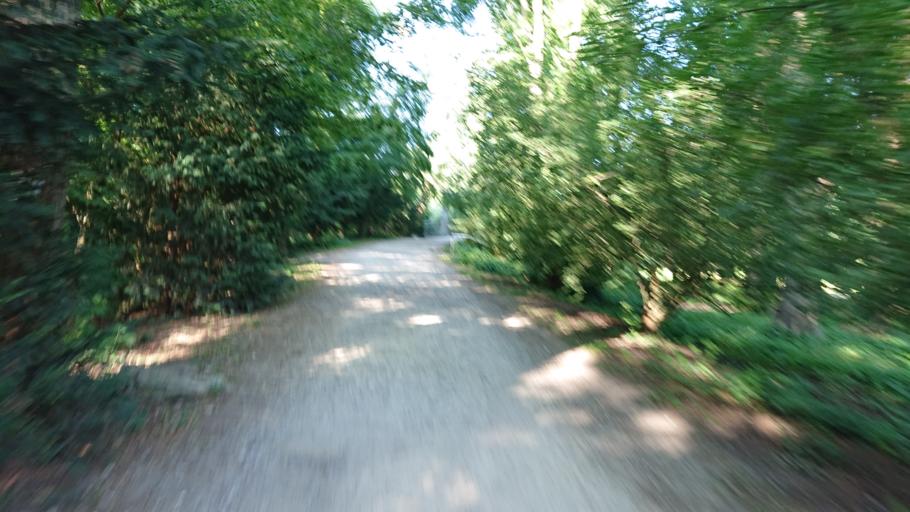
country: DE
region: Brandenburg
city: Potsdam
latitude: 52.3953
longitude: 13.0714
